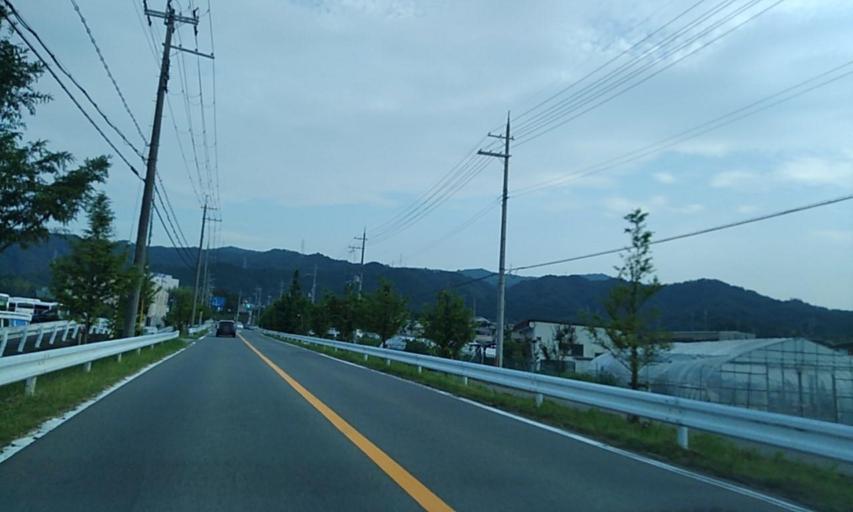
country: JP
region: Kyoto
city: Kameoka
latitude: 34.9978
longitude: 135.6043
